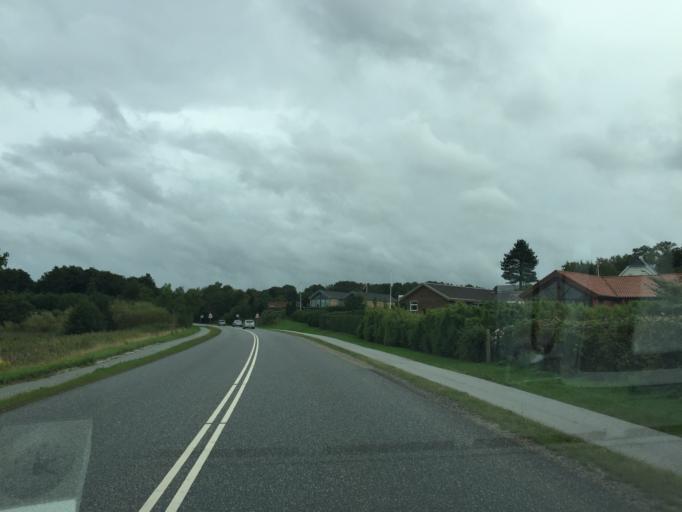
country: DK
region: South Denmark
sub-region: Kolding Kommune
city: Kolding
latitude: 55.4828
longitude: 9.5110
